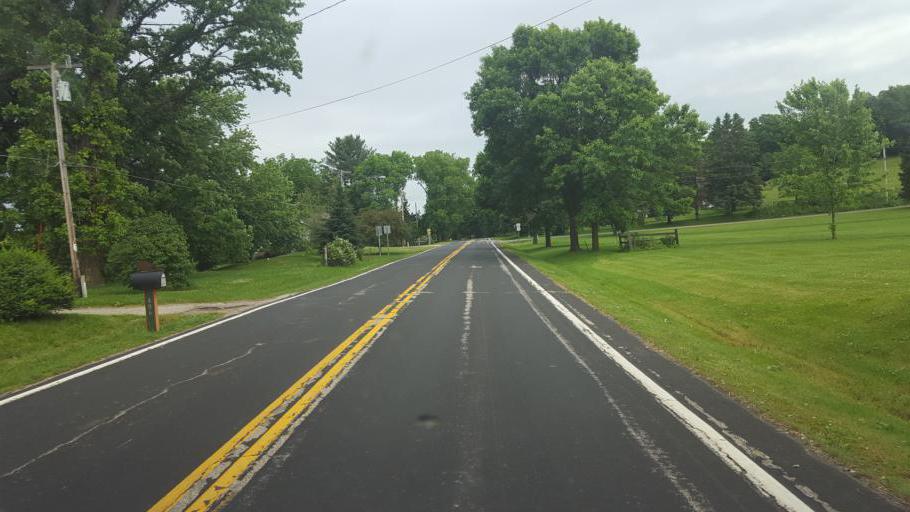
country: US
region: Wisconsin
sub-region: Monroe County
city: Cashton
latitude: 43.7188
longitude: -90.5858
